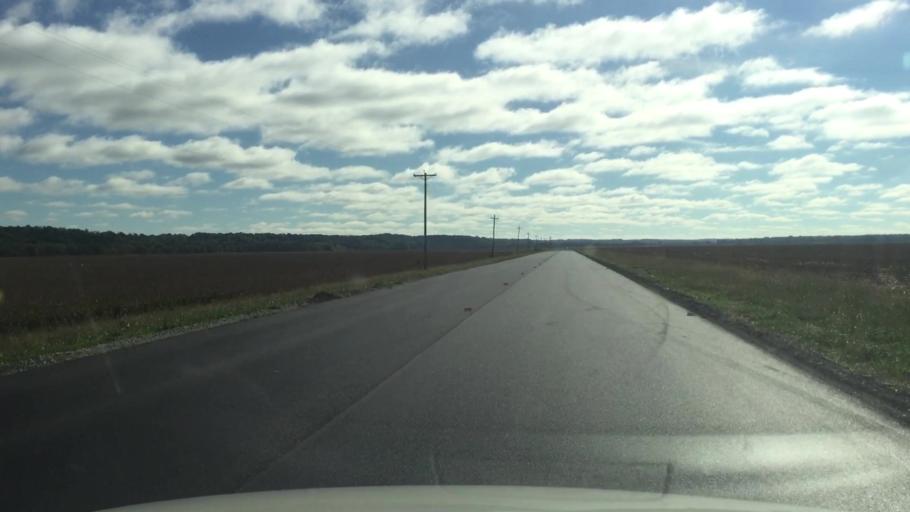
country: US
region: Missouri
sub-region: Howard County
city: New Franklin
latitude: 38.9949
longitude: -92.6581
